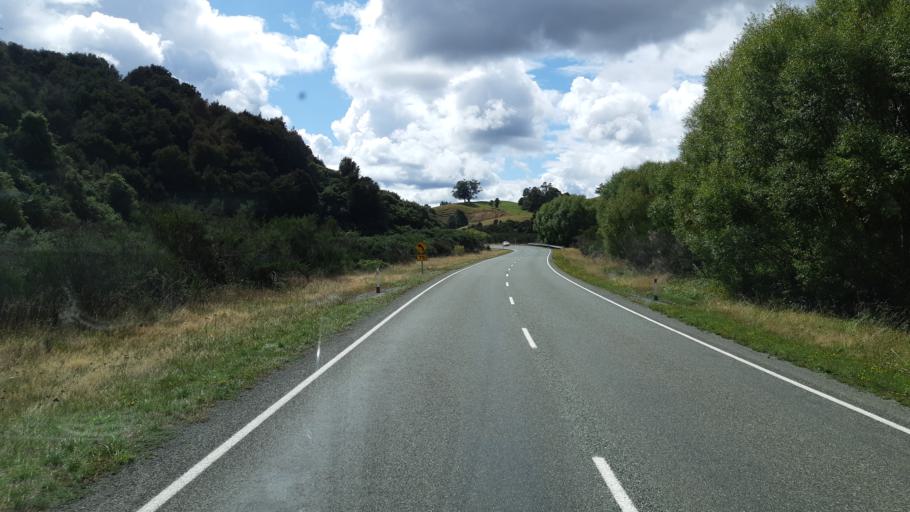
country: NZ
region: Tasman
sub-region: Tasman District
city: Wakefield
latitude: -41.6461
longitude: 172.6555
